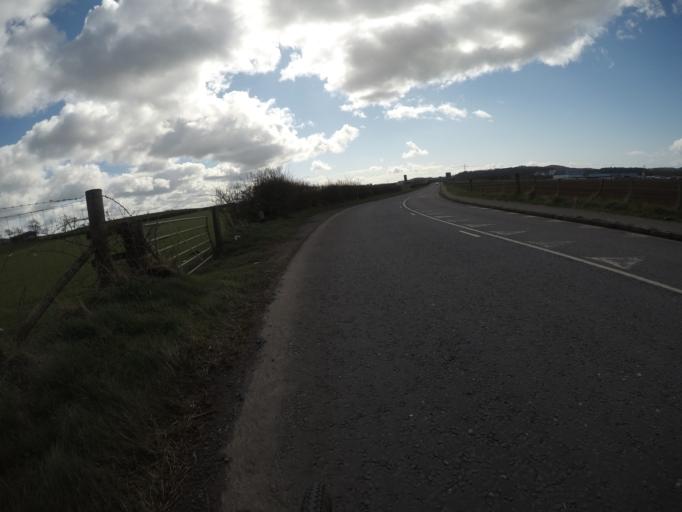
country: GB
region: Scotland
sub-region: North Ayrshire
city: Dreghorn
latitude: 55.5938
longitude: -4.6032
